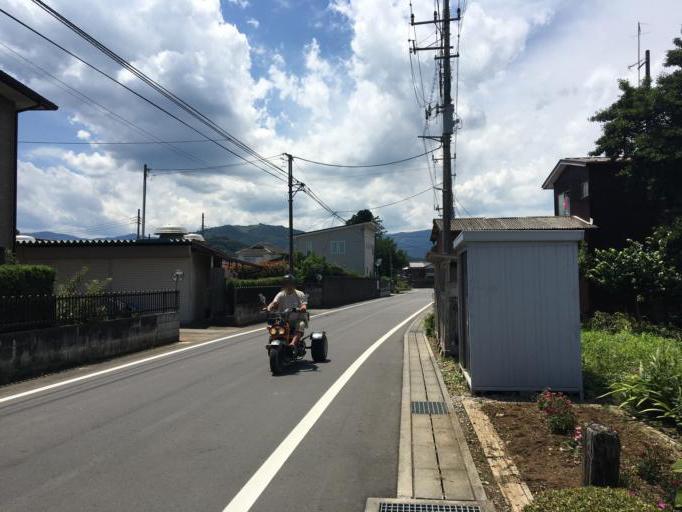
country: JP
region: Saitama
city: Ogawa
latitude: 36.0033
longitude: 139.2920
